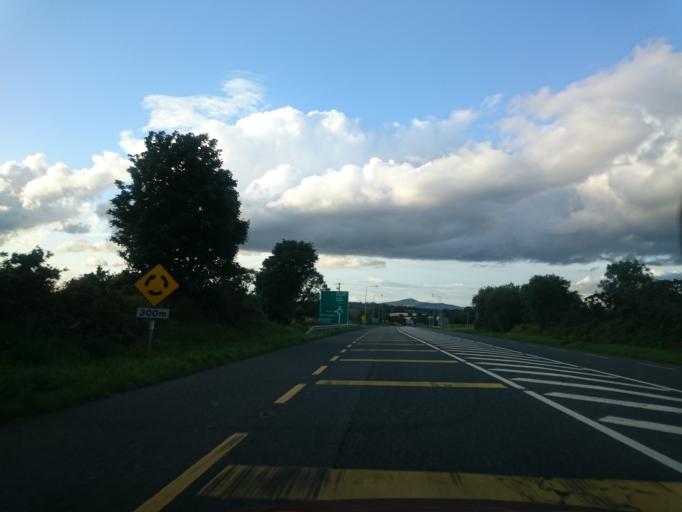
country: IE
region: Leinster
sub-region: Loch Garman
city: Enniscorthy
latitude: 52.5408
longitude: -6.5519
